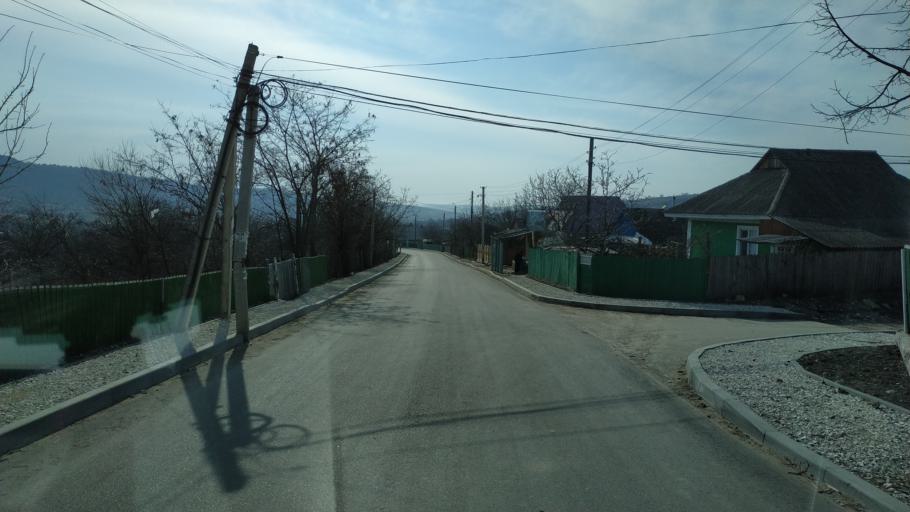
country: MD
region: Nisporeni
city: Nisporeni
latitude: 47.1679
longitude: 28.1308
